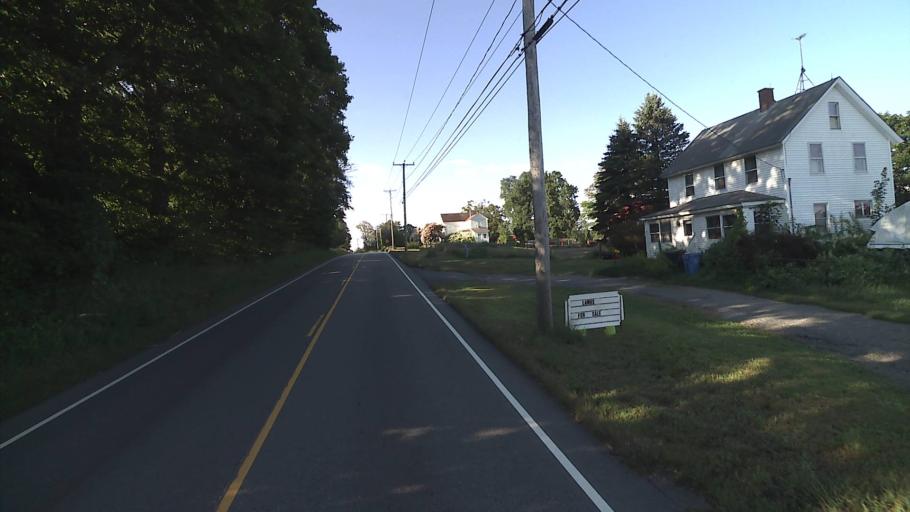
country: US
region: Connecticut
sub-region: Windham County
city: South Windham
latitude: 41.6475
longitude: -72.1606
